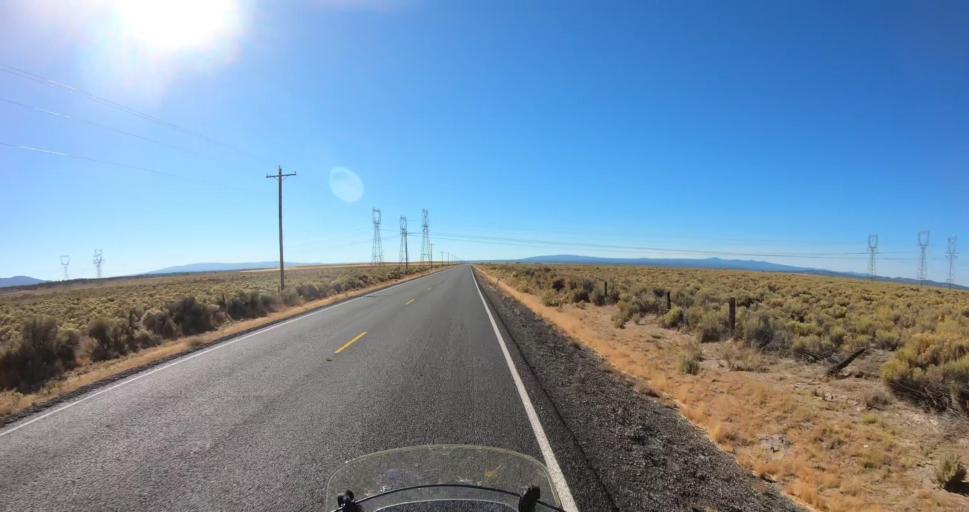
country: US
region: Oregon
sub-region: Deschutes County
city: La Pine
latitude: 43.1294
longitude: -120.9460
